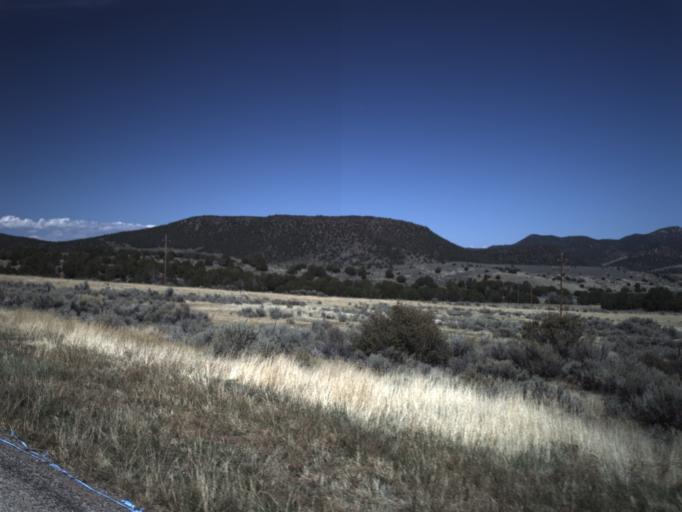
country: US
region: Utah
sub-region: Washington County
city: Enterprise
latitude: 37.5155
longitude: -113.6350
